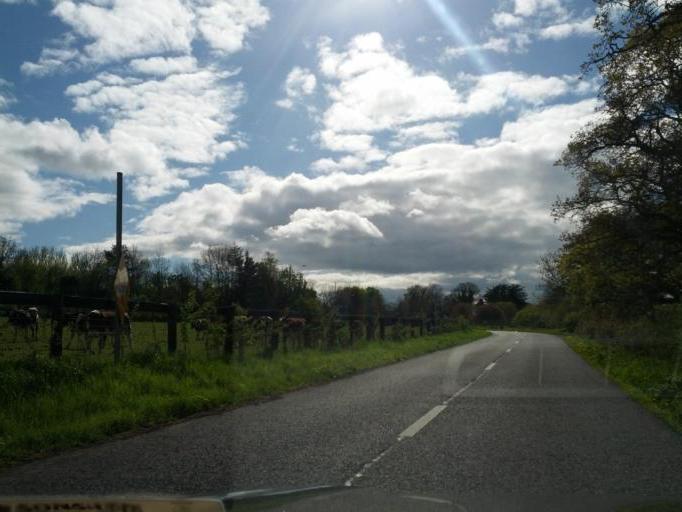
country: IE
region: Leinster
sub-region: Kildare
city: Kilcock
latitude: 53.4790
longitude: -6.7128
